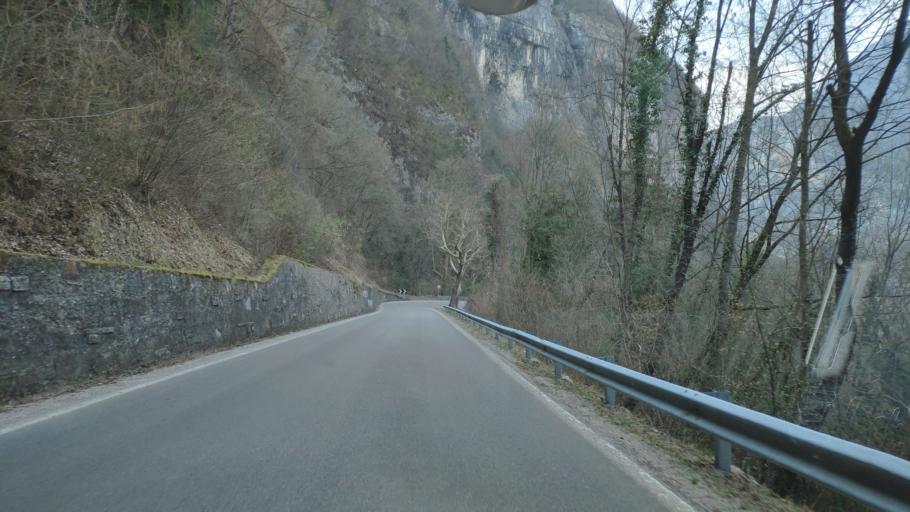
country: IT
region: Veneto
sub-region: Provincia di Vicenza
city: Enego
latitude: 45.9542
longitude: 11.7095
